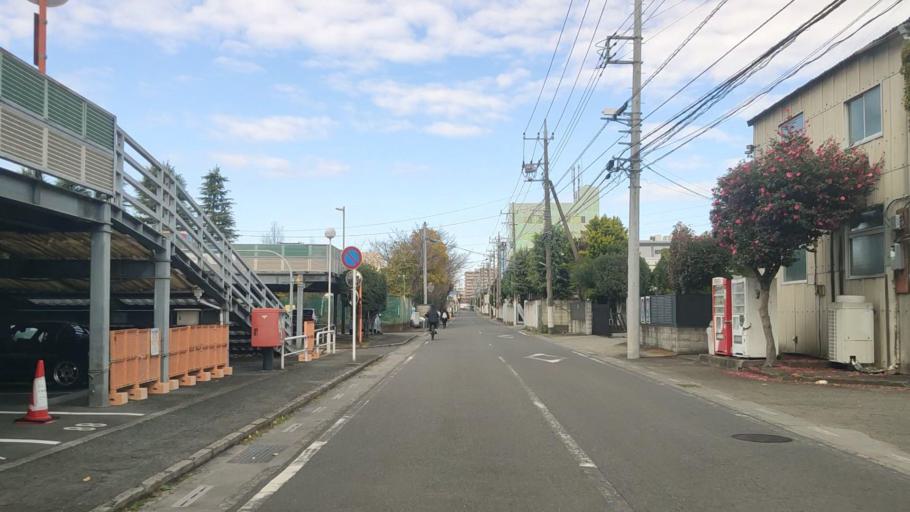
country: JP
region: Kanagawa
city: Minami-rinkan
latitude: 35.4983
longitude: 139.4318
